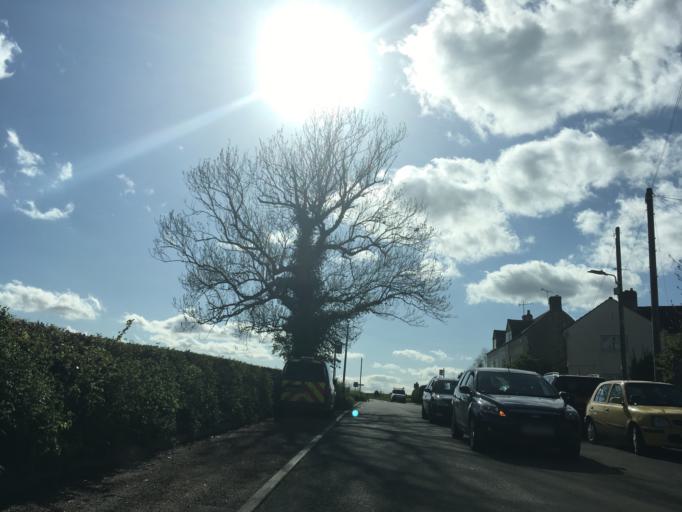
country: GB
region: England
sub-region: Gloucestershire
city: Stonehouse
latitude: 51.7294
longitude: -2.2921
